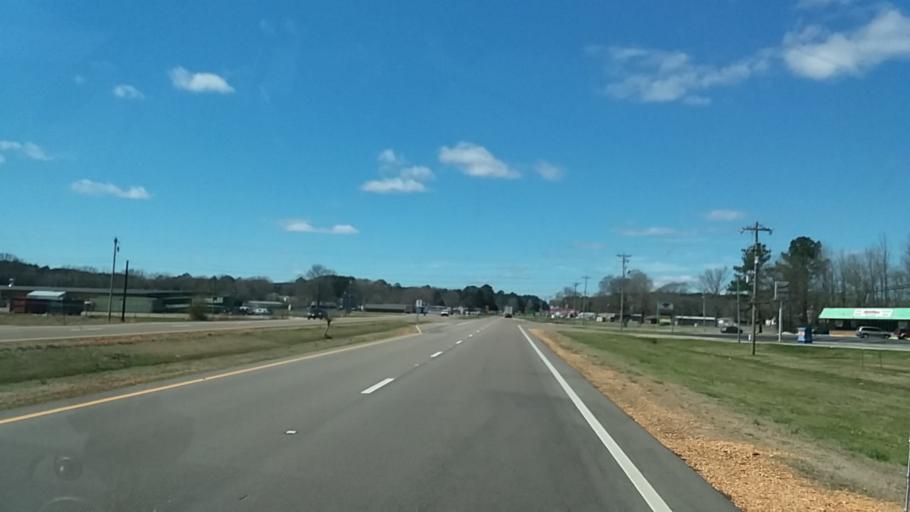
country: US
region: Mississippi
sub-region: Tishomingo County
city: Iuka
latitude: 34.8328
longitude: -88.3117
